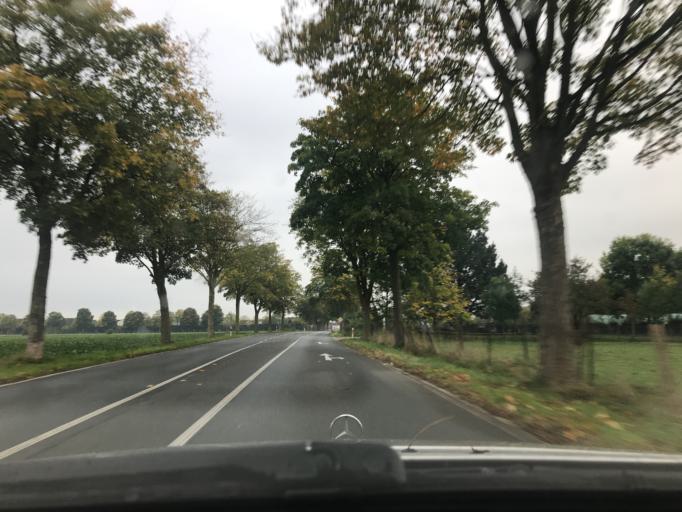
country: DE
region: North Rhine-Westphalia
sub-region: Regierungsbezirk Dusseldorf
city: Moers
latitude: 51.4245
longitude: 6.5797
